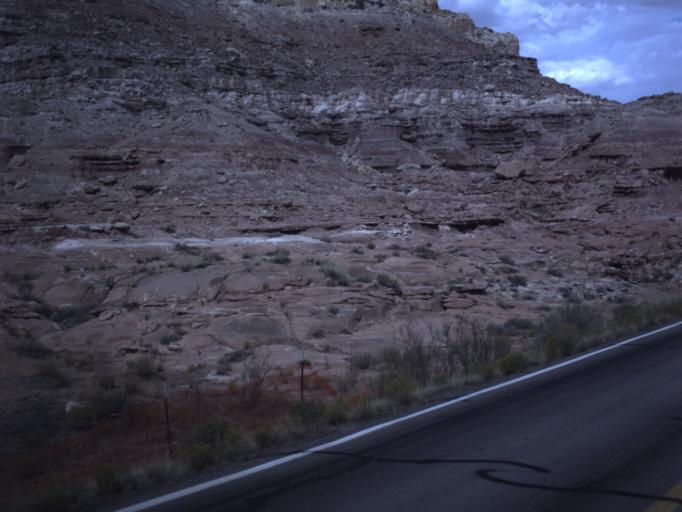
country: US
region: Utah
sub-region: San Juan County
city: Blanding
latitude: 37.2576
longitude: -109.2823
